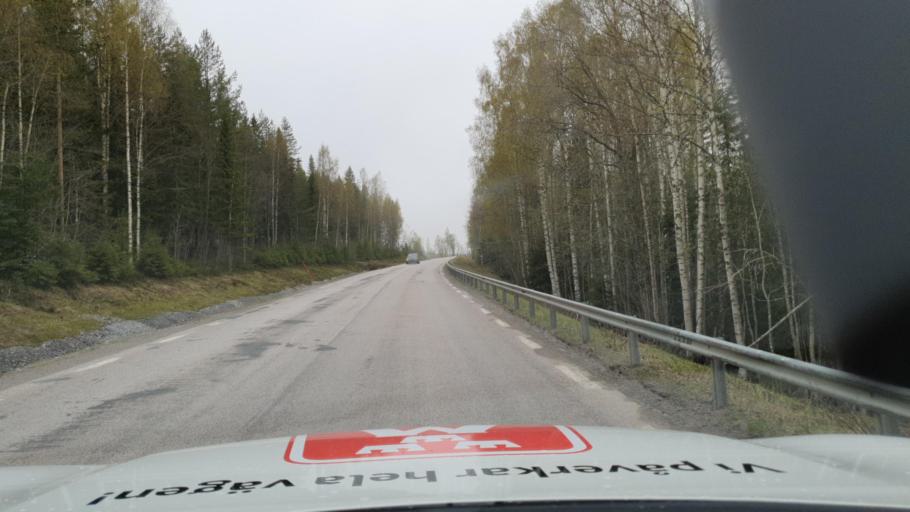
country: SE
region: Vaesterbotten
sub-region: Vannas Kommun
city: Vaennaes
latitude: 63.7879
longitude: 19.8283
